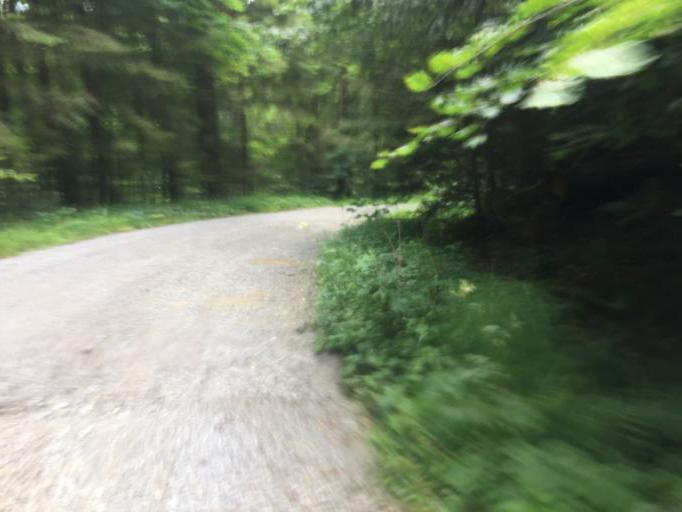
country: CH
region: Bern
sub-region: Thun District
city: Wattenwil
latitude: 46.7516
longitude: 7.4847
